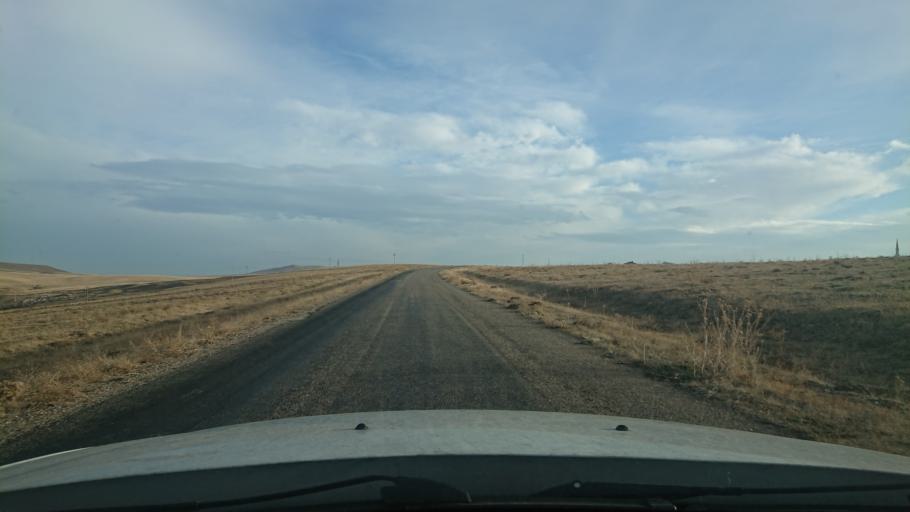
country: TR
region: Aksaray
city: Acipinar
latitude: 38.6592
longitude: 33.8395
